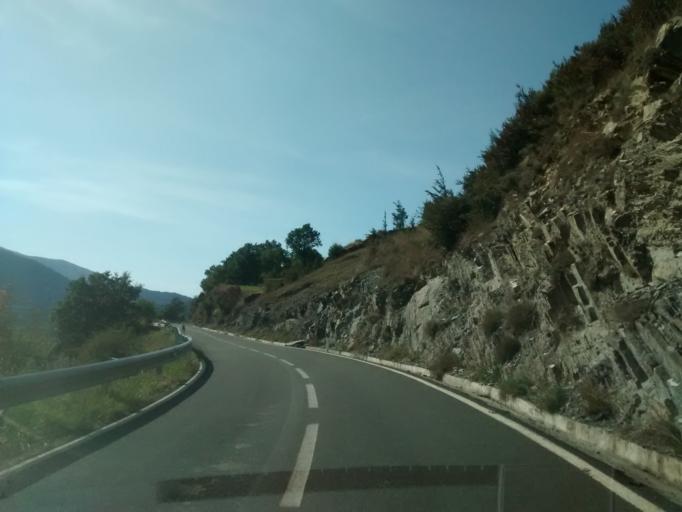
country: ES
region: Aragon
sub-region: Provincia de Huesca
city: Broto
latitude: 42.6143
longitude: -0.1248
